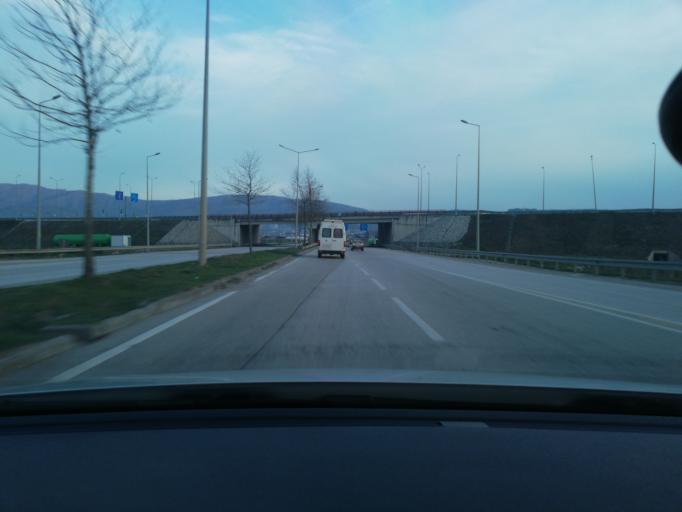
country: TR
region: Duzce
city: Konuralp
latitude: 40.8858
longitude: 31.1703
